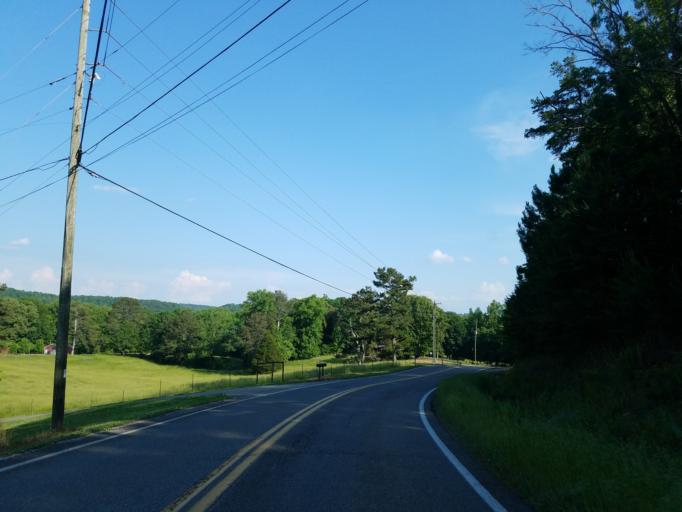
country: US
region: Georgia
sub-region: Pickens County
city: Nelson
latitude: 34.3763
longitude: -84.3564
